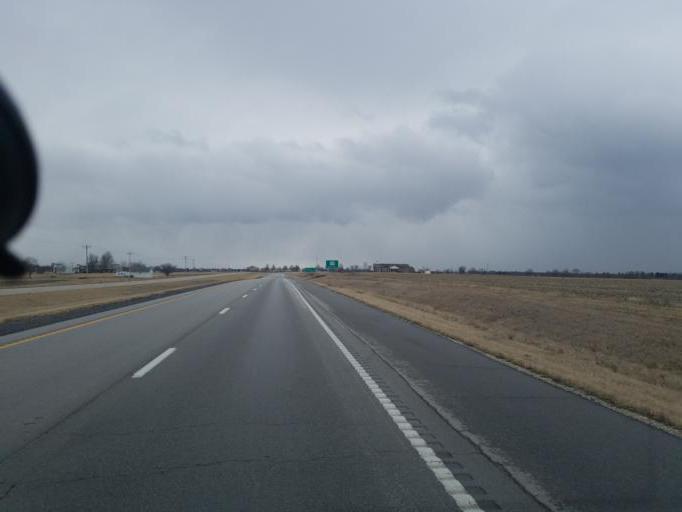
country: US
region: Missouri
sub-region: Macon County
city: Macon
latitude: 39.8056
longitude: -92.4746
